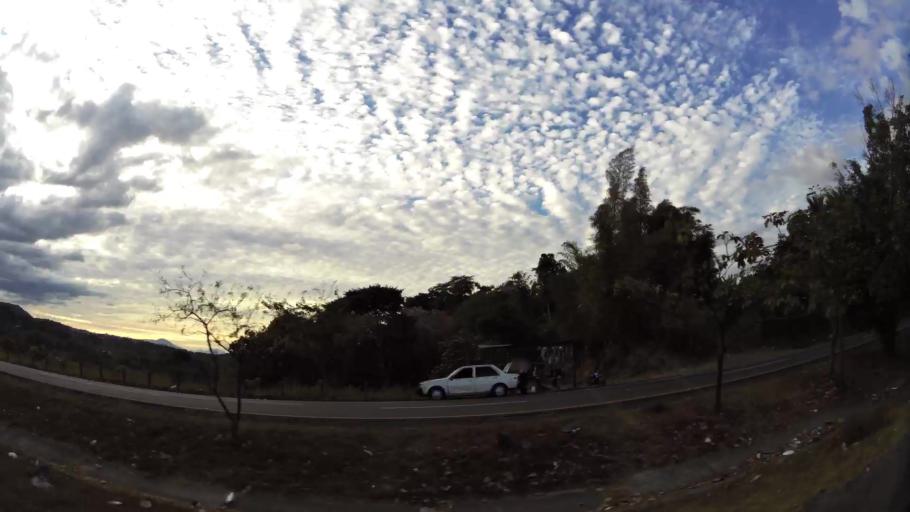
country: SV
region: Cuscatlan
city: Cojutepeque
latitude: 13.7259
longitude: -88.9002
